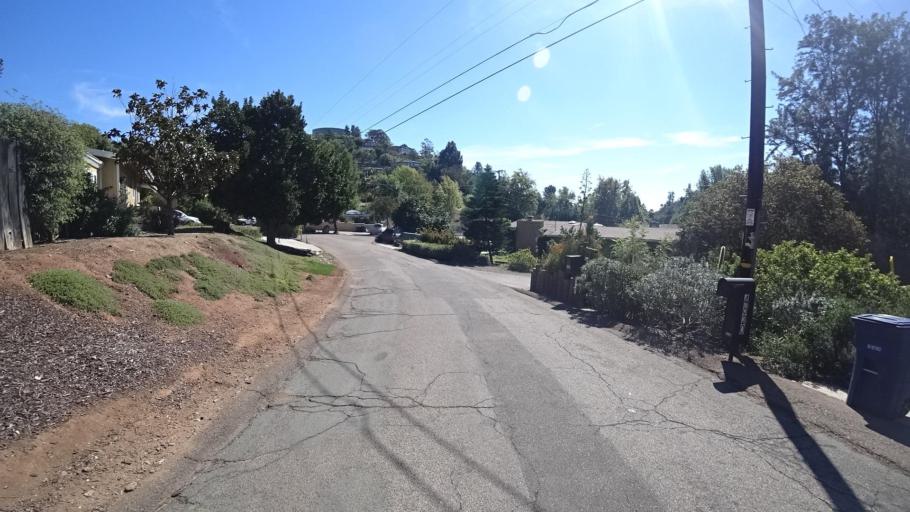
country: US
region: California
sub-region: San Diego County
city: Casa de Oro-Mount Helix
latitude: 32.7621
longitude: -116.9702
